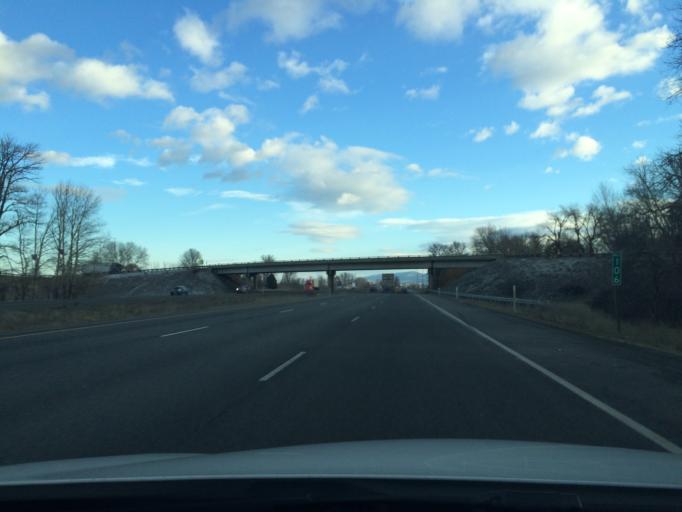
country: US
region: Washington
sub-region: Kittitas County
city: Ellensburg
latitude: 47.0068
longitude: -120.5925
